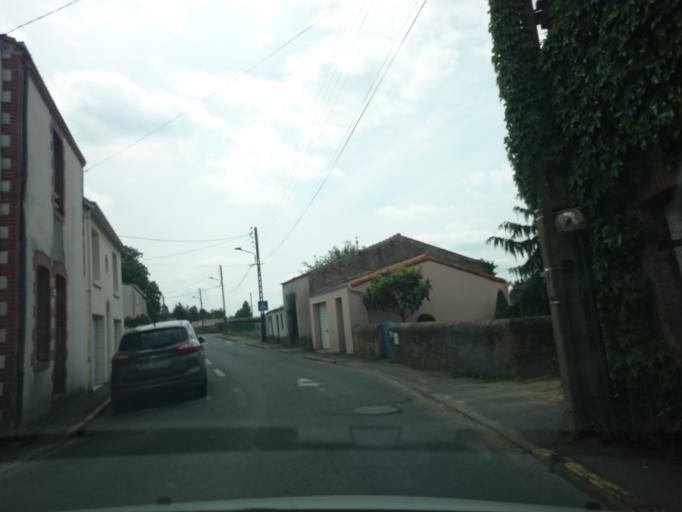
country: FR
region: Pays de la Loire
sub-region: Departement de la Loire-Atlantique
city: La Chevroliere
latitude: 47.0939
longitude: -1.6132
